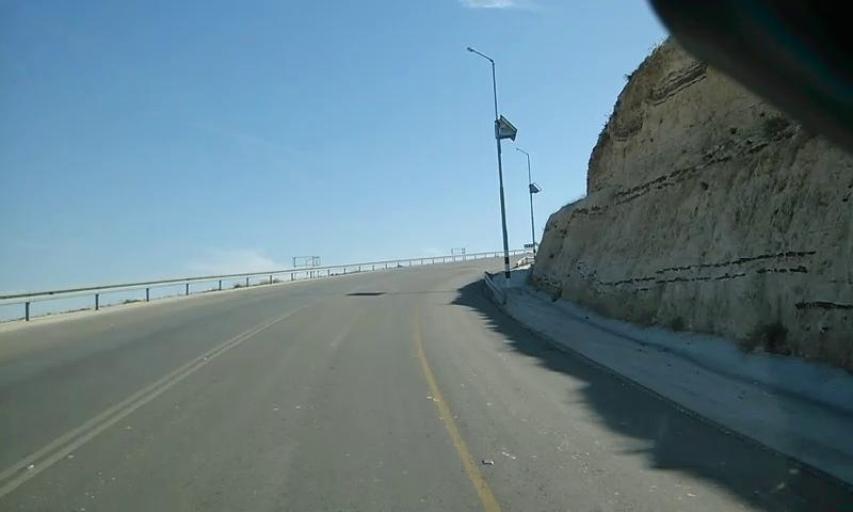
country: PS
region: West Bank
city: Al `Ayzariyah
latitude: 31.7501
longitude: 35.2949
